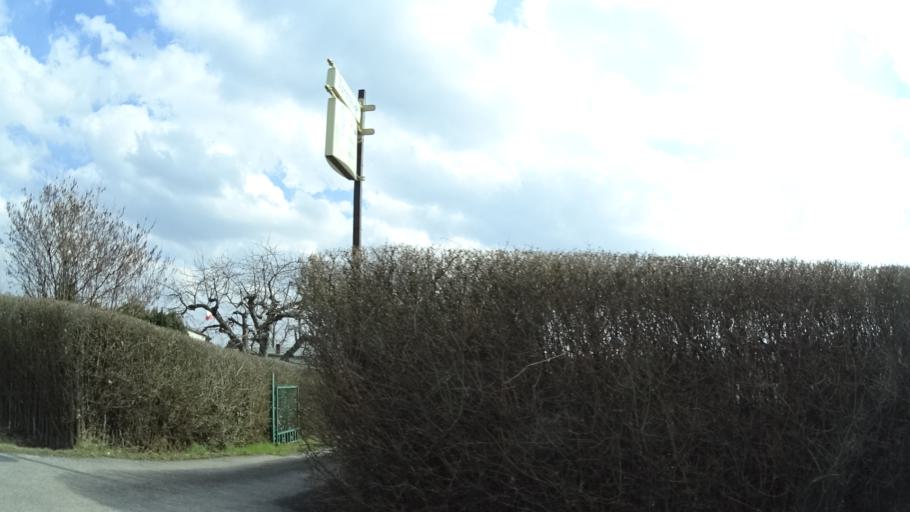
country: DE
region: Thuringia
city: Apolda
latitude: 51.0330
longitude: 11.5014
